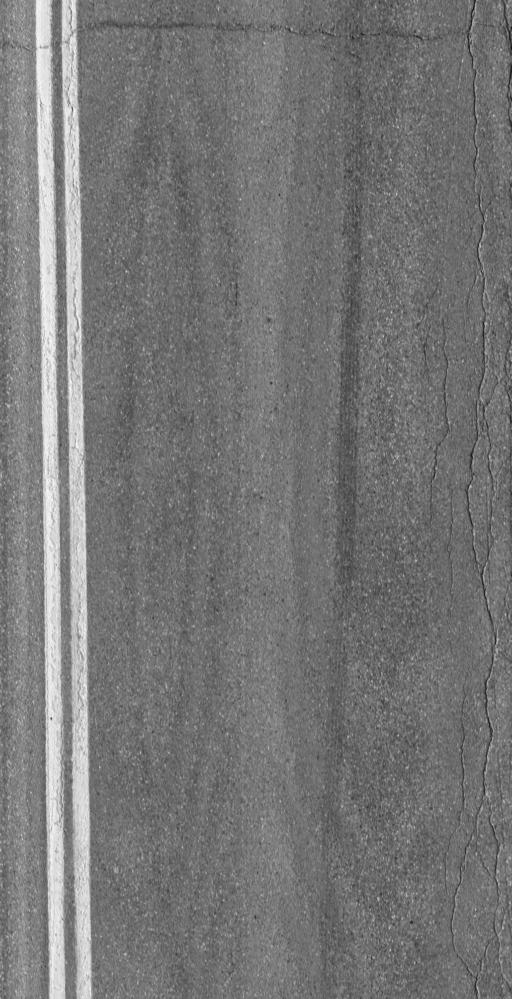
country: US
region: Vermont
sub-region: Chittenden County
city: Williston
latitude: 44.4222
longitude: -73.1068
